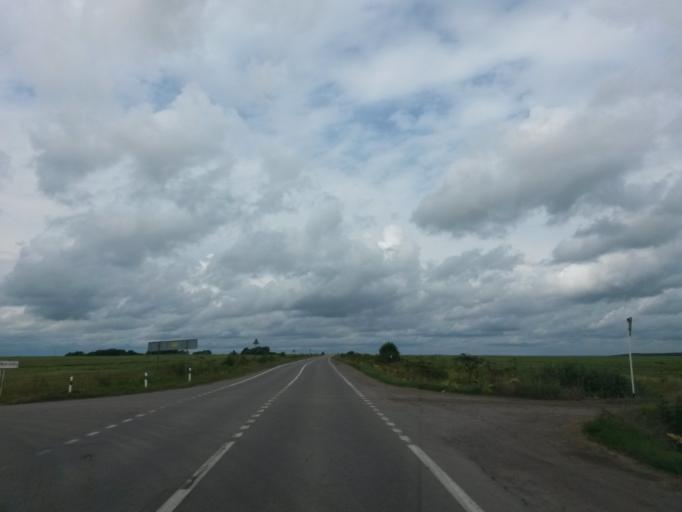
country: RU
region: Jaroslavl
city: Yaroslavl
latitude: 57.7516
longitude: 39.8764
